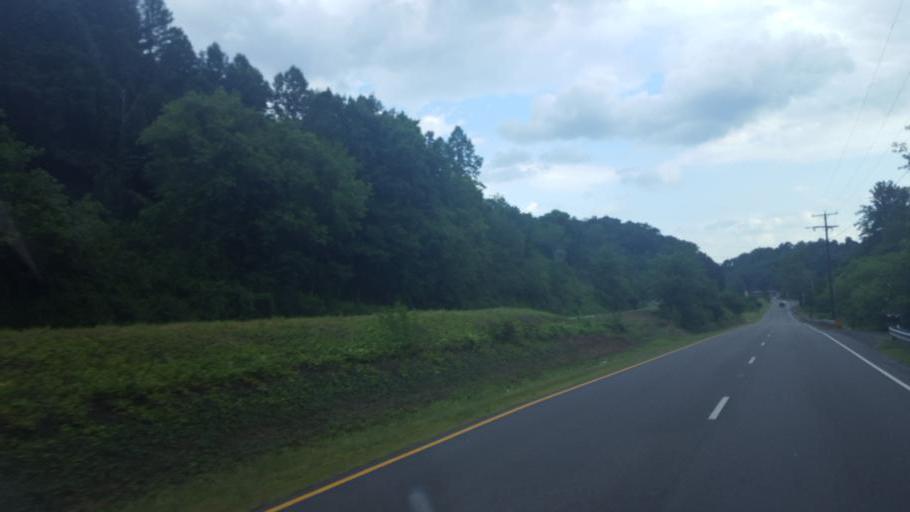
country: US
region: Virginia
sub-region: Wise County
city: Pound
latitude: 37.0963
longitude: -82.6002
